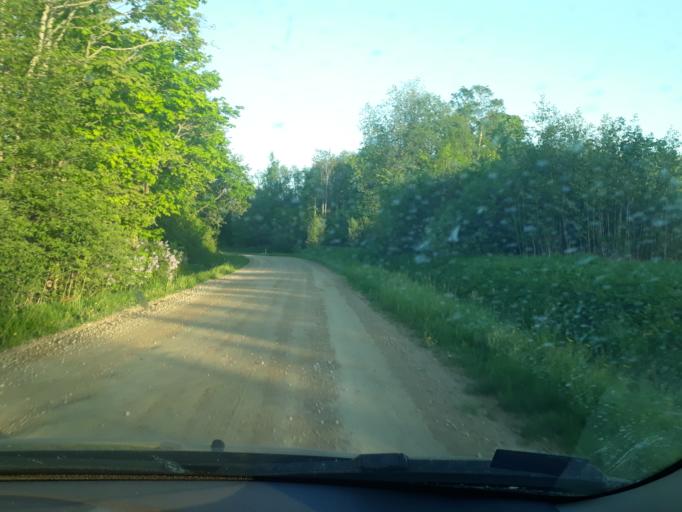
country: EE
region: Paernumaa
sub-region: Vaendra vald (alev)
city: Vandra
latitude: 58.5664
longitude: 24.9482
